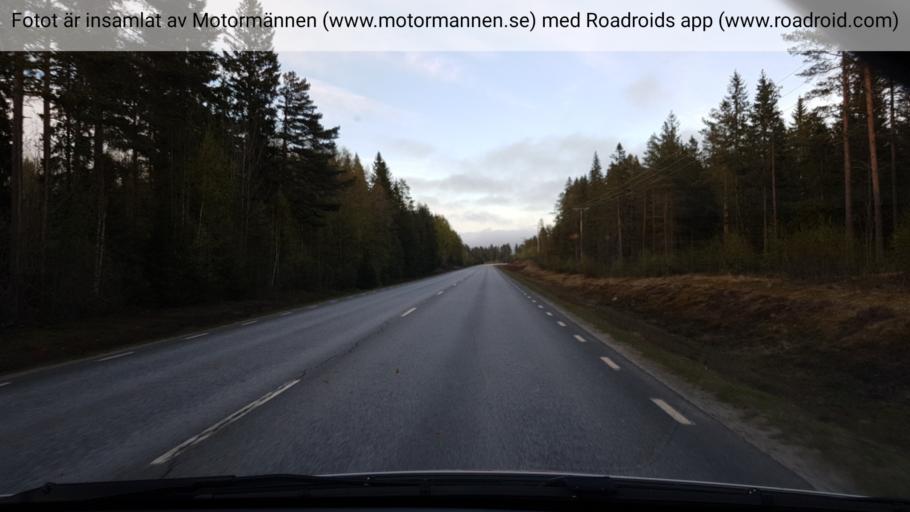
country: SE
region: Vaesterbotten
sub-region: Umea Kommun
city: Roback
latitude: 63.7733
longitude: 20.0116
